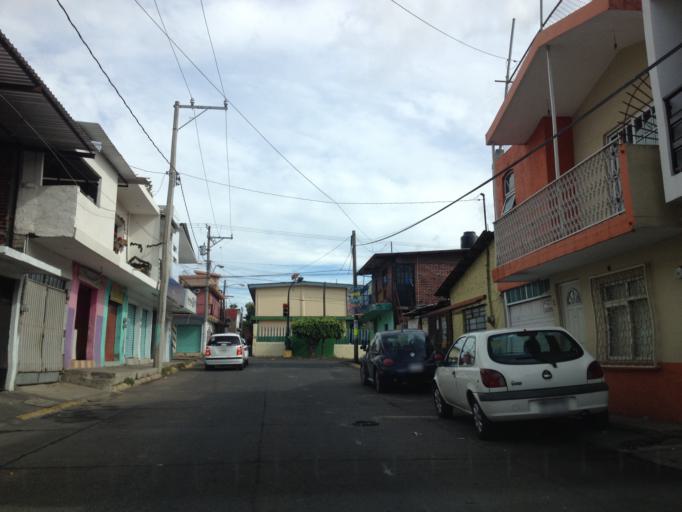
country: MX
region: Michoacan
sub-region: Uruapan
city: Uruapan
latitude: 19.4084
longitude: -102.0592
